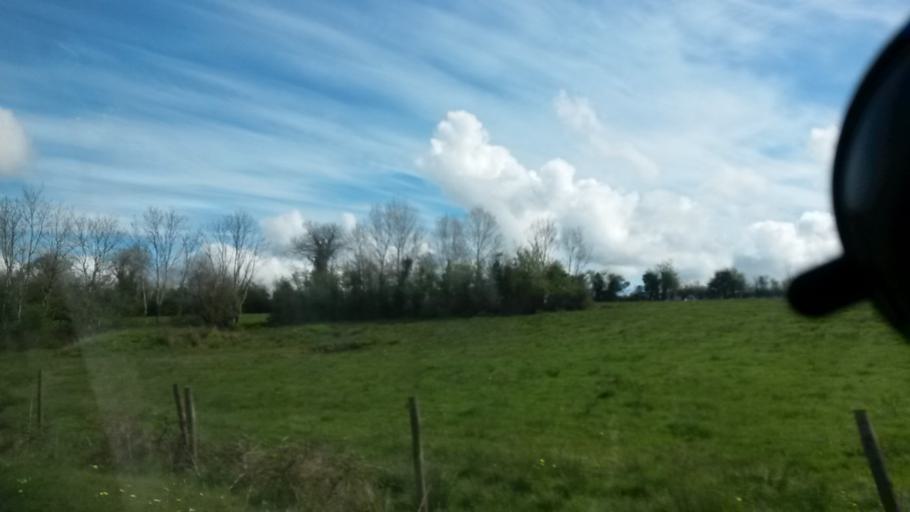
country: IE
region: Ulster
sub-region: An Cabhan
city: Belturbet
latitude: 54.1732
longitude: -7.5048
